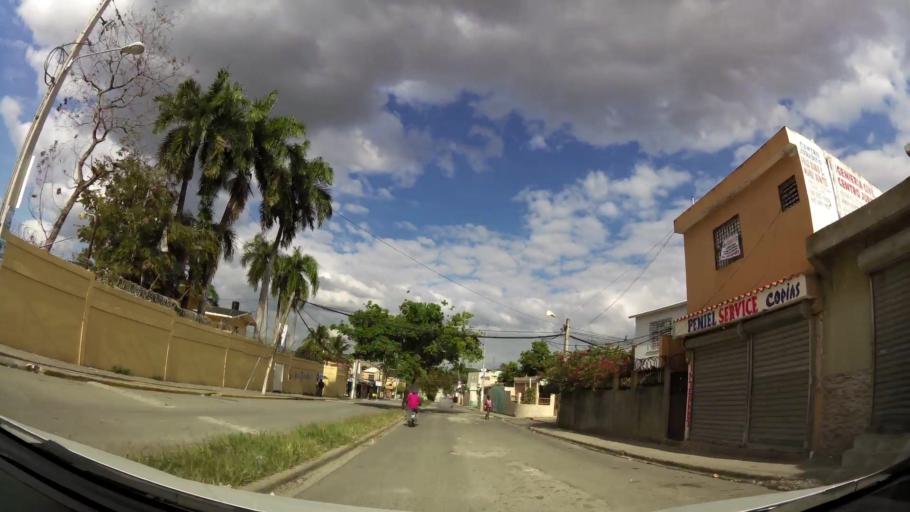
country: DO
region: Nacional
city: Ensanche Luperon
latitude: 18.5543
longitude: -69.9032
